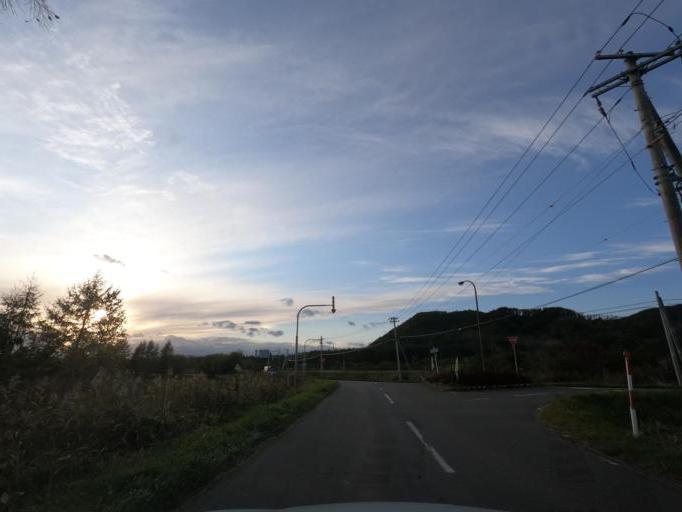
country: JP
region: Hokkaido
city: Obihiro
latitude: 42.5770
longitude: 143.3269
